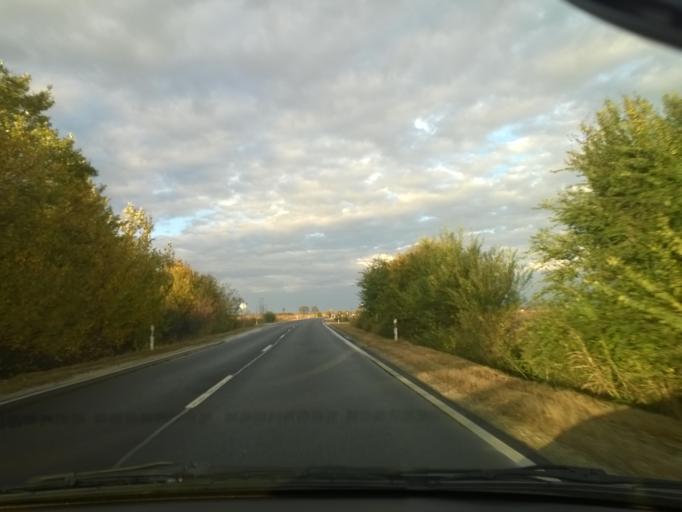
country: HU
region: Bacs-Kiskun
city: Dunapataj
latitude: 46.6089
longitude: 18.9853
